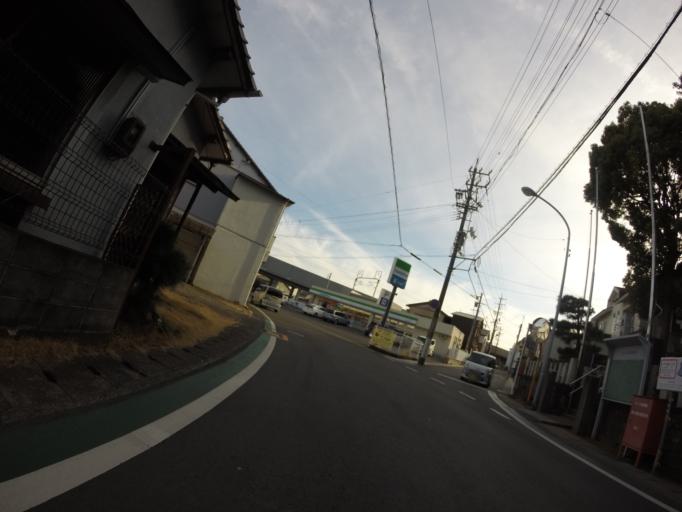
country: JP
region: Shizuoka
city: Shizuoka-shi
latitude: 35.0358
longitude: 138.4830
